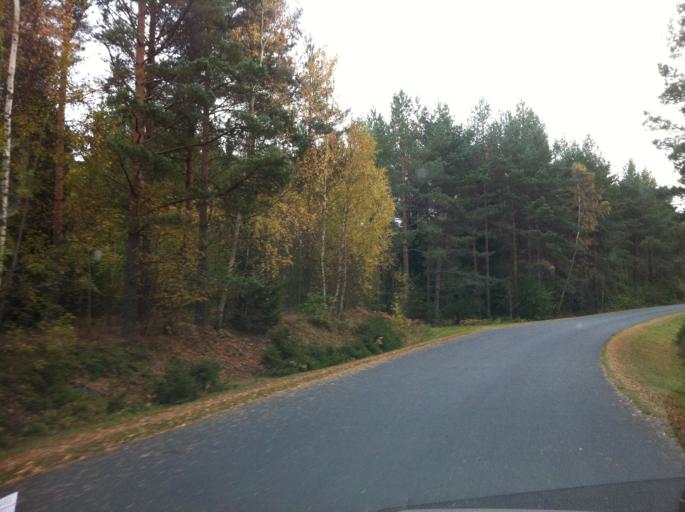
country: SE
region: OEstergoetland
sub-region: Motala Kommun
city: Motala
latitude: 58.6176
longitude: 14.9550
